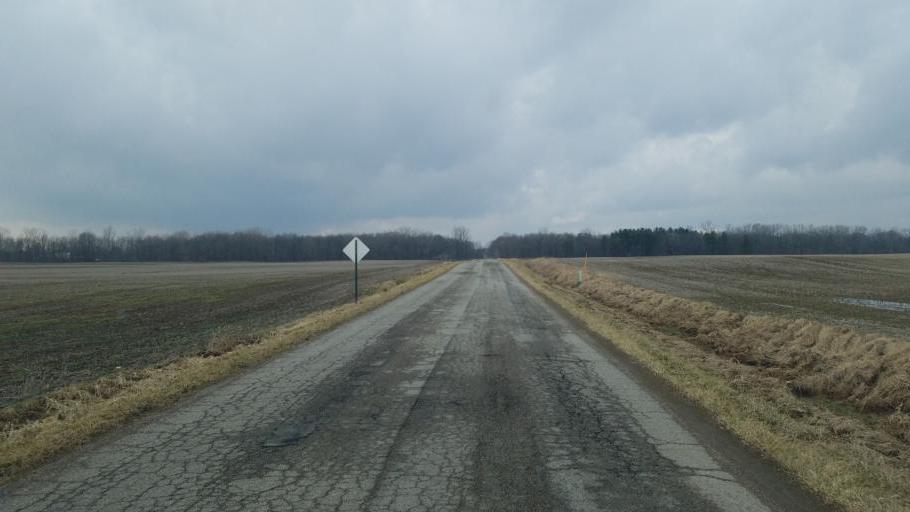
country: US
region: Ohio
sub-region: Knox County
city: Fredericktown
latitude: 40.4900
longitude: -82.6876
